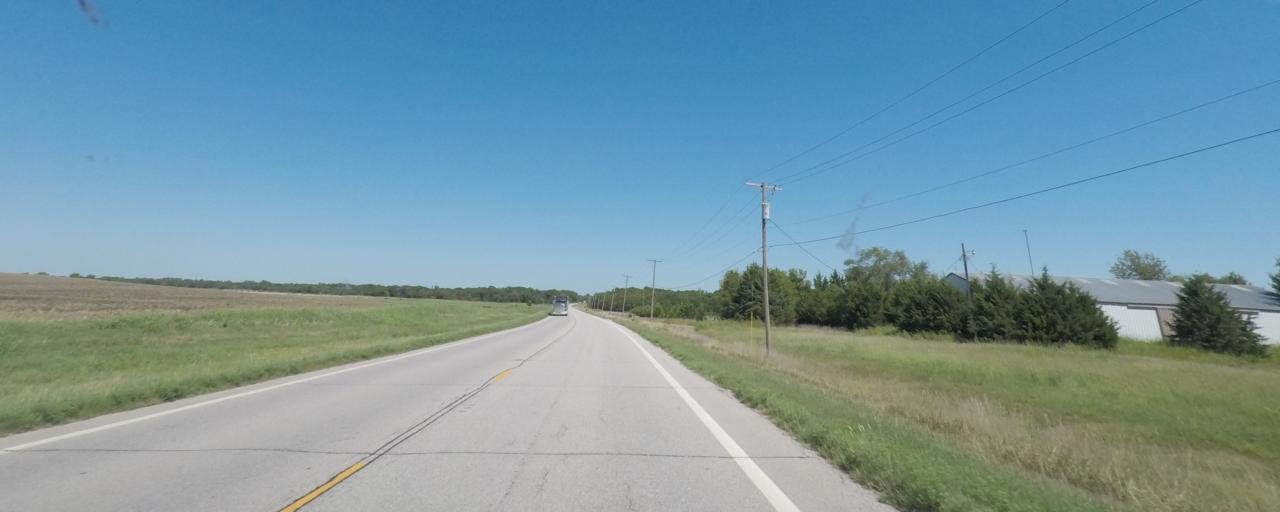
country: US
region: Kansas
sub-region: Sumner County
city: Wellington
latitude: 37.2420
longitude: -97.4028
